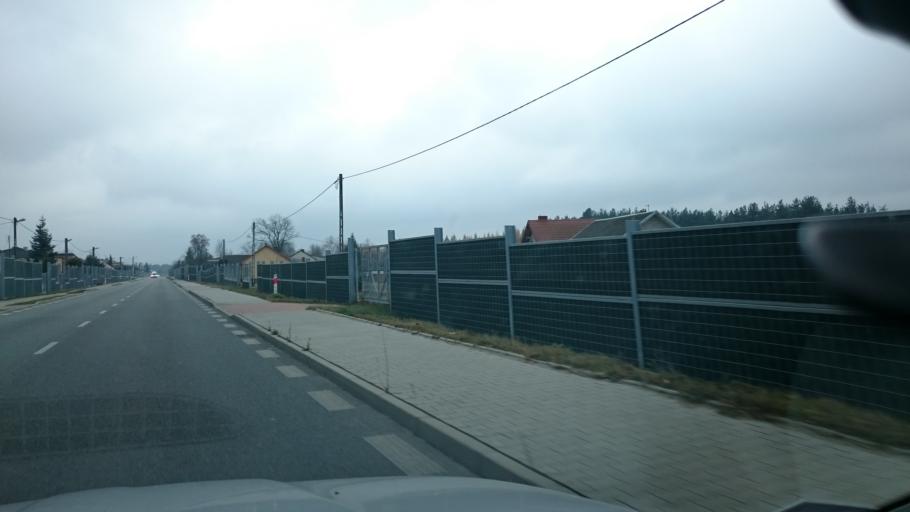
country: PL
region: Swietokrzyskie
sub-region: Powiat konecki
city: Konskie
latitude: 51.1481
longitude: 20.3621
